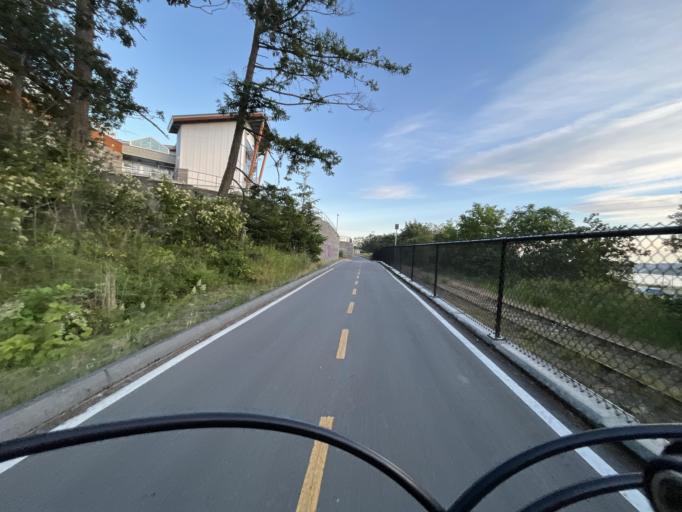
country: CA
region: British Columbia
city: Colwood
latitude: 48.4419
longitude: -123.4293
